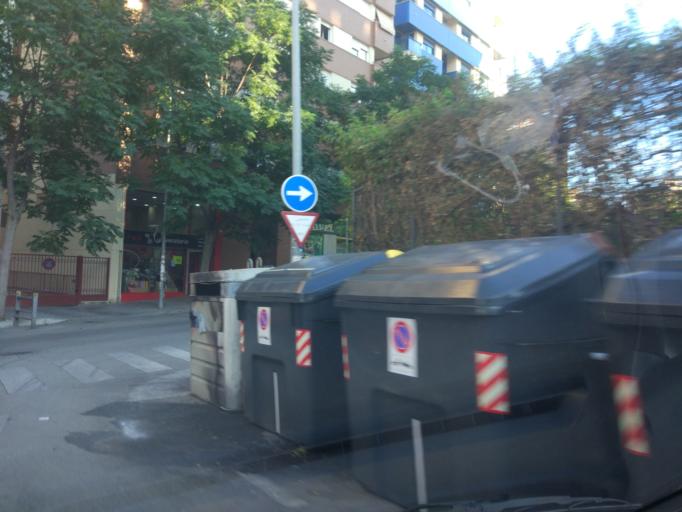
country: ES
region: Andalusia
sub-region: Provincia de Jaen
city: Jaen
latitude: 37.7855
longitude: -3.7778
